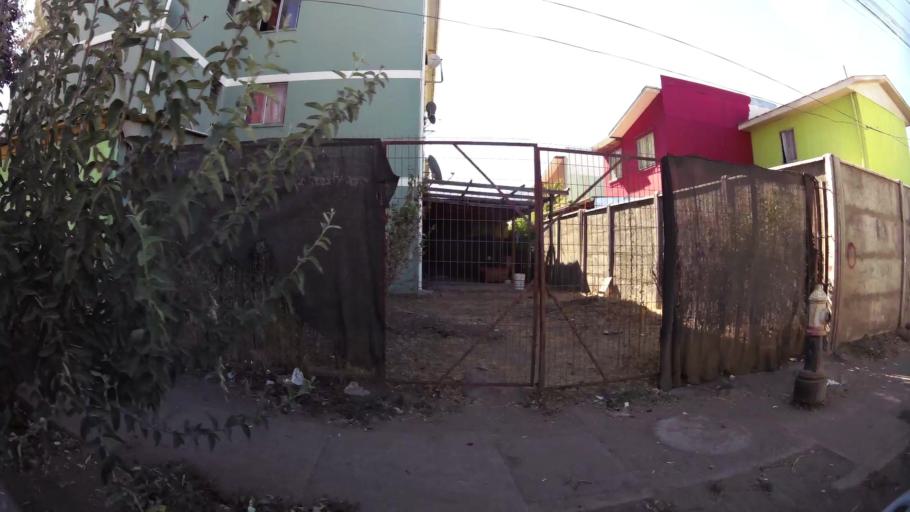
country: CL
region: O'Higgins
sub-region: Provincia de Colchagua
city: Chimbarongo
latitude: -34.5746
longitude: -71.0035
